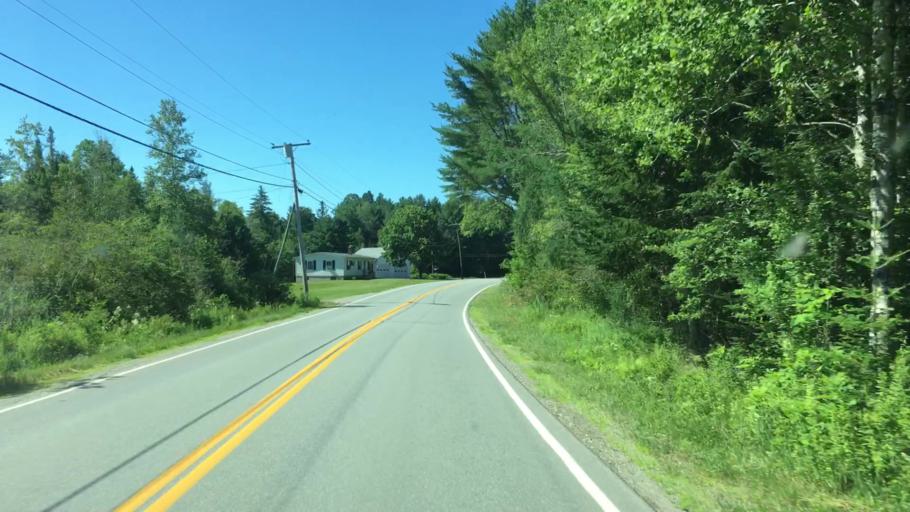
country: US
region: Maine
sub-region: Hancock County
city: Dedham
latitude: 44.7218
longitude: -68.6397
